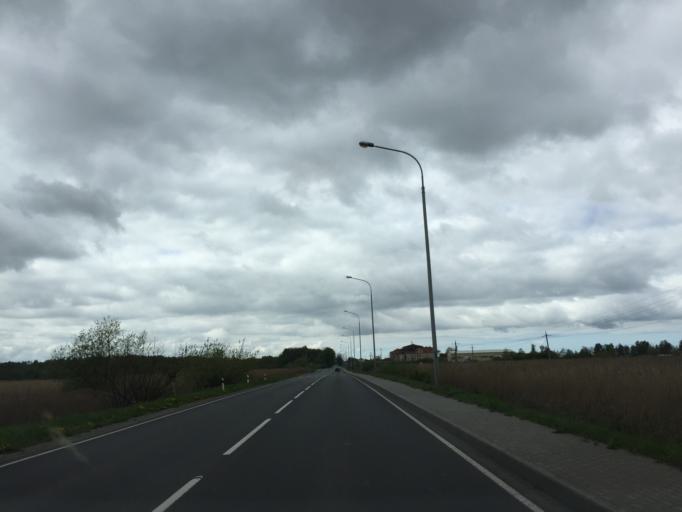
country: RU
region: Kaliningrad
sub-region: Gorod Kaliningrad
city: Kaliningrad
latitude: 54.6615
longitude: 20.4049
